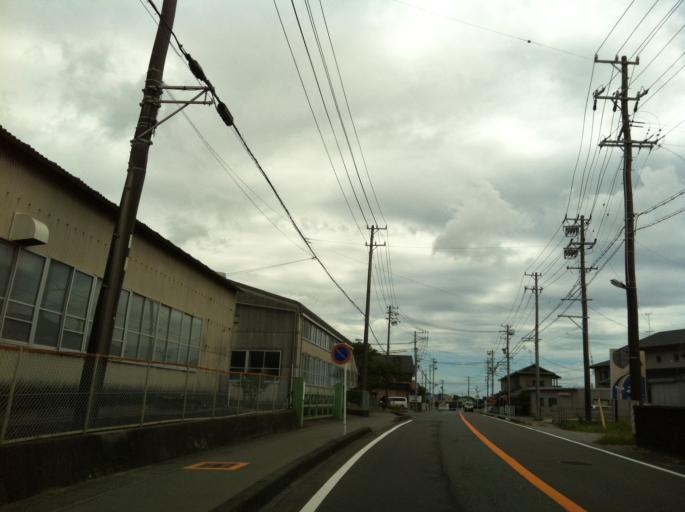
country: JP
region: Shizuoka
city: Kakegawa
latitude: 34.6788
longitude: 137.9957
